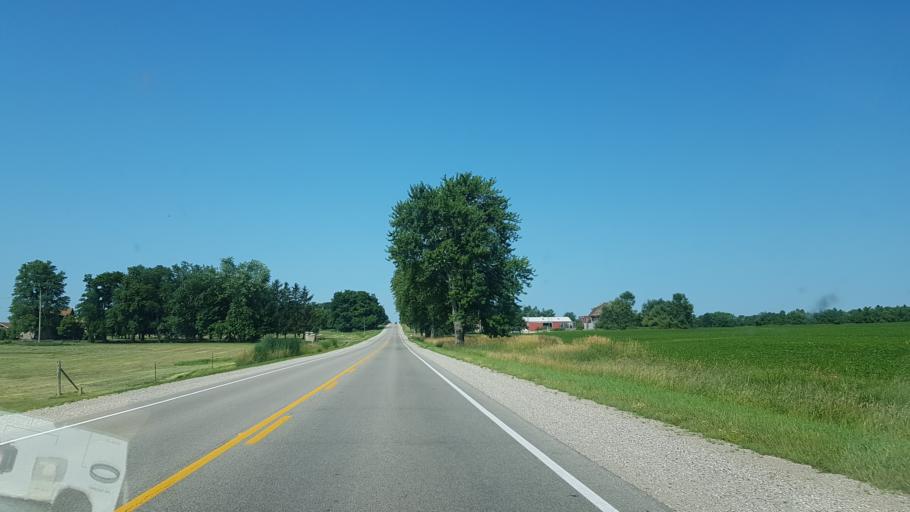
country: CA
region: Ontario
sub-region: Oxford County
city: Woodstock
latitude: 43.0198
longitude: -80.6785
